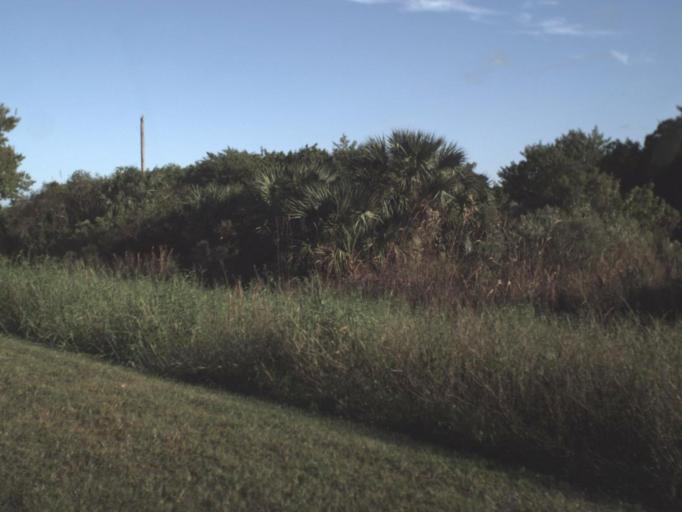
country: US
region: Florida
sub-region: Brevard County
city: Merritt Island
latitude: 28.6435
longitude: -80.6905
